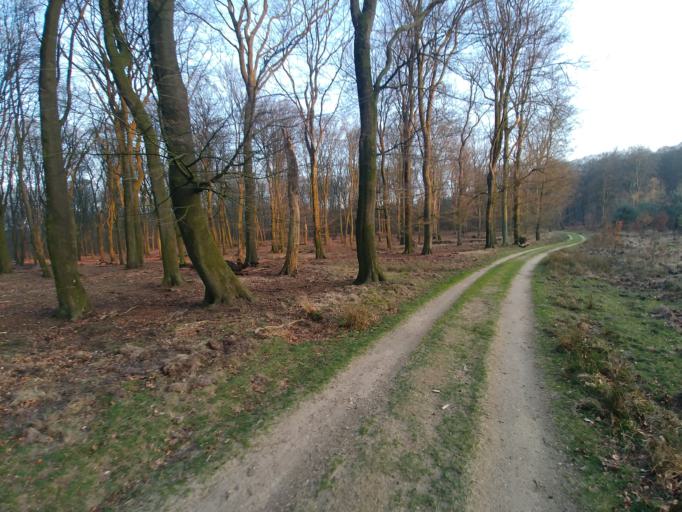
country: NL
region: Gelderland
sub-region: Gemeente Epe
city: Vaassen
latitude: 52.3137
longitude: 5.8762
